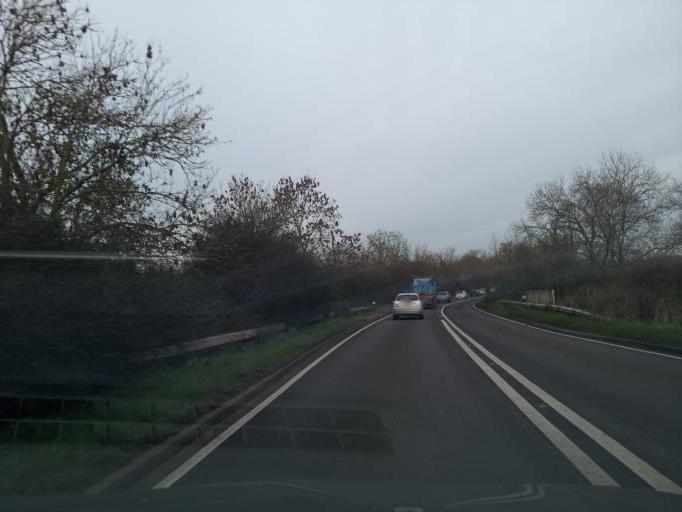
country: GB
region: England
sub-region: Buckinghamshire
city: Aylesbury
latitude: 51.8501
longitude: -0.7732
